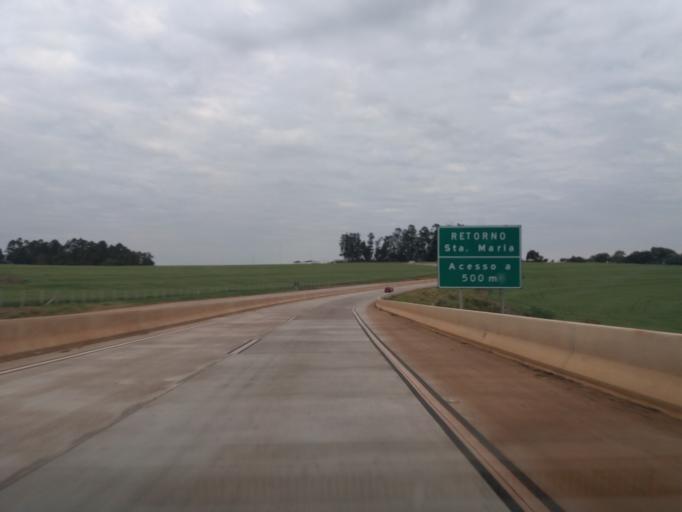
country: BR
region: Parana
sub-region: Cascavel
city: Cascavel
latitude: -25.1419
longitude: -53.5912
